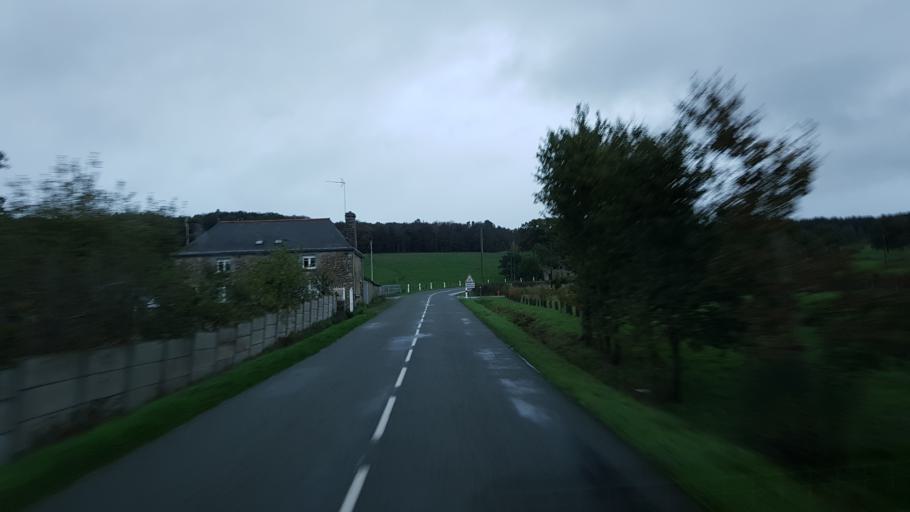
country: FR
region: Pays de la Loire
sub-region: Departement de la Mayenne
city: Juvigne
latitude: 48.2151
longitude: -1.0470
